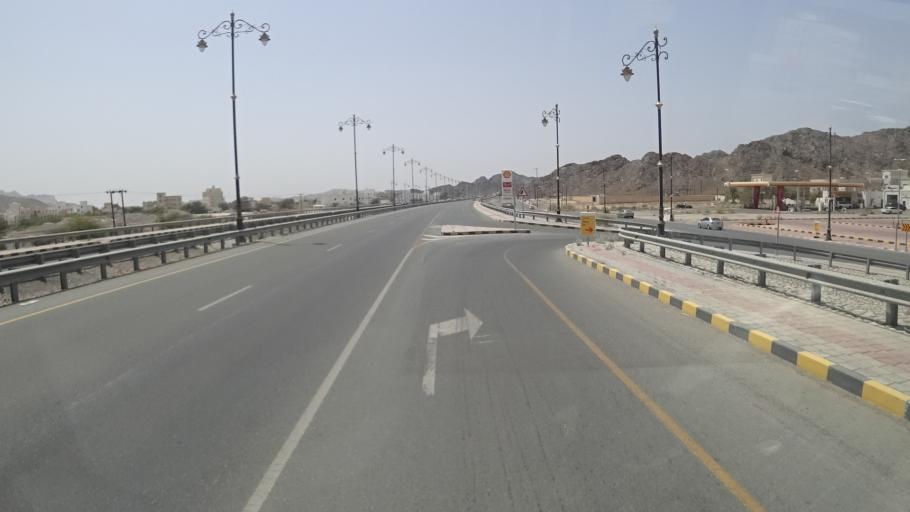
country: OM
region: Muhafazat ad Dakhiliyah
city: Nizwa
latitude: 22.9691
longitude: 57.5436
